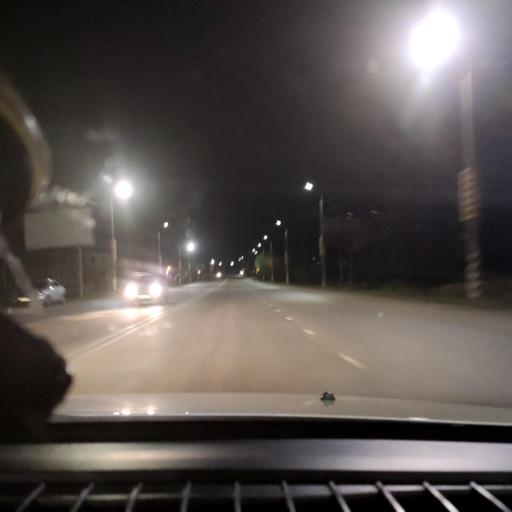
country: RU
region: Samara
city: Novokuybyshevsk
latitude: 53.0821
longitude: 49.9593
